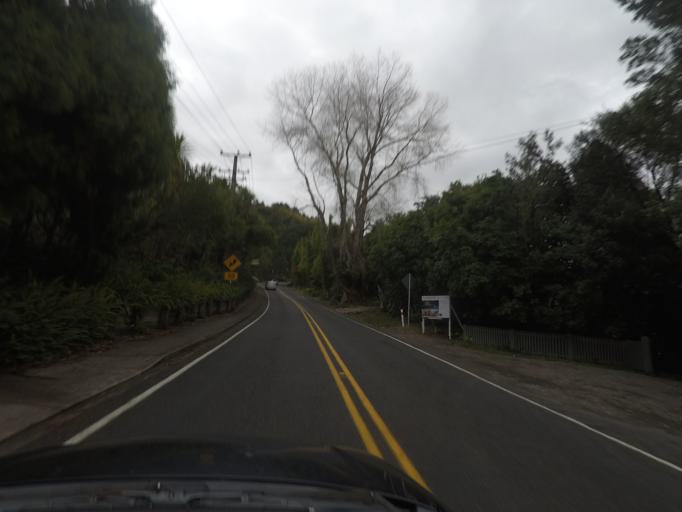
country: NZ
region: Auckland
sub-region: Auckland
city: Titirangi
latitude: -36.9322
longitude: 174.5895
